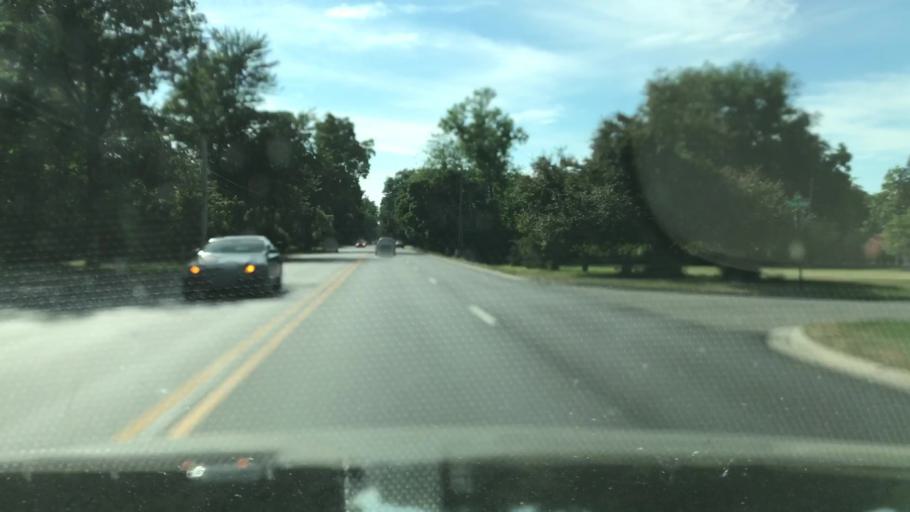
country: US
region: Michigan
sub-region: Kent County
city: East Grand Rapids
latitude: 42.9580
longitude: -85.5953
